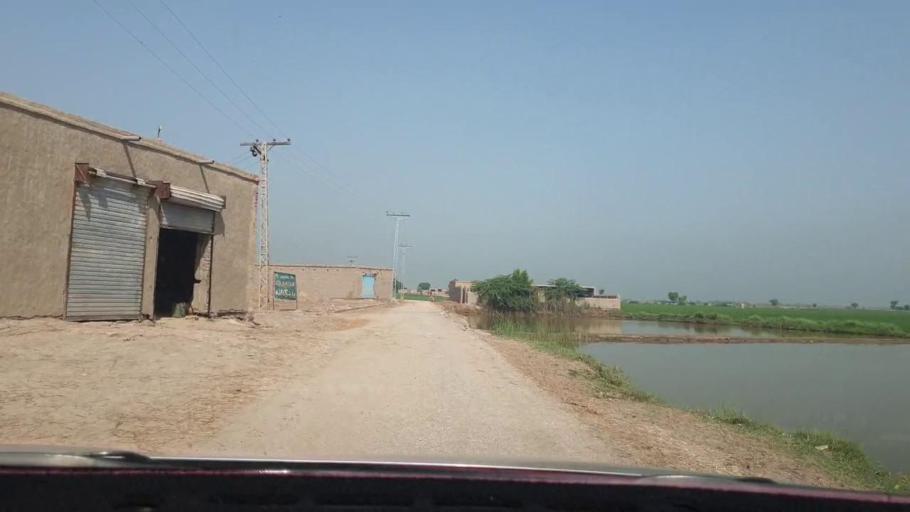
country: PK
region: Sindh
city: Nasirabad
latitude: 27.4233
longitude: 67.9103
